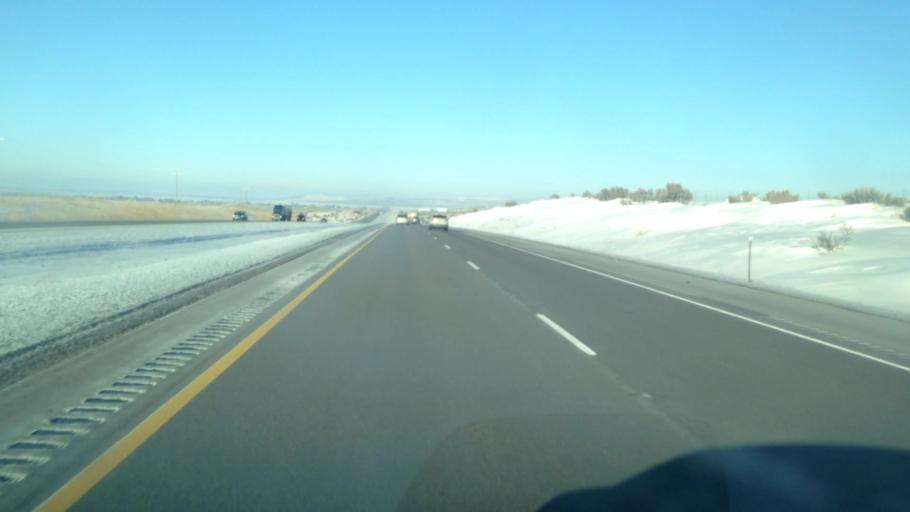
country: US
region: Idaho
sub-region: Bingham County
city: Fort Hall
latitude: 42.9733
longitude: -112.4237
